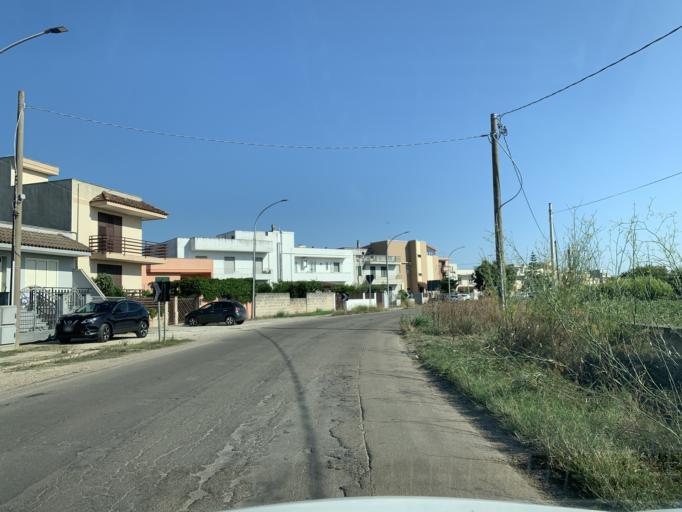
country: IT
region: Apulia
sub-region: Provincia di Lecce
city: Nardo
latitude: 40.1875
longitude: 18.0279
